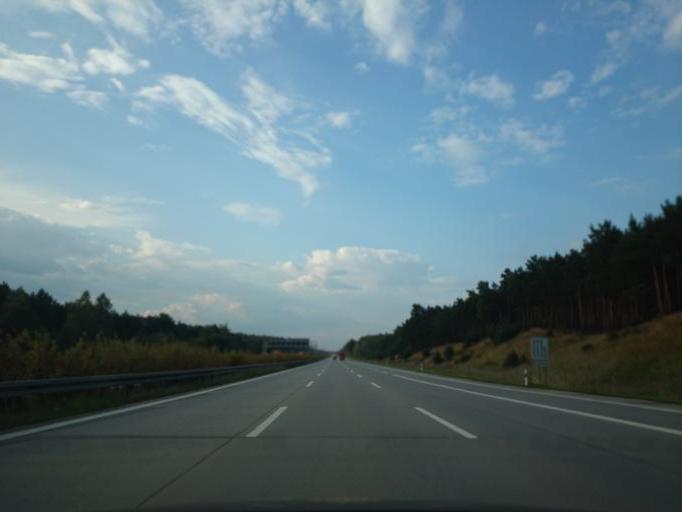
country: DE
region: Brandenburg
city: Erkner
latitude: 52.3303
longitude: 13.7511
